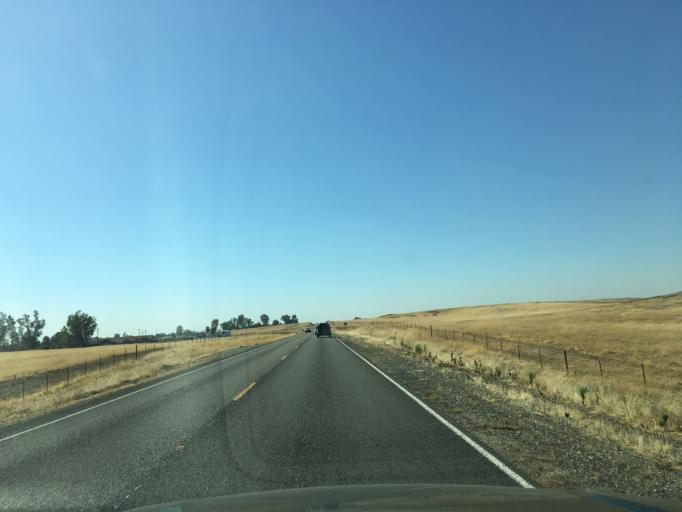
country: US
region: California
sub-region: Madera County
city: Bonadelle Ranchos-Madera Ranchos
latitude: 37.0103
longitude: -119.8536
